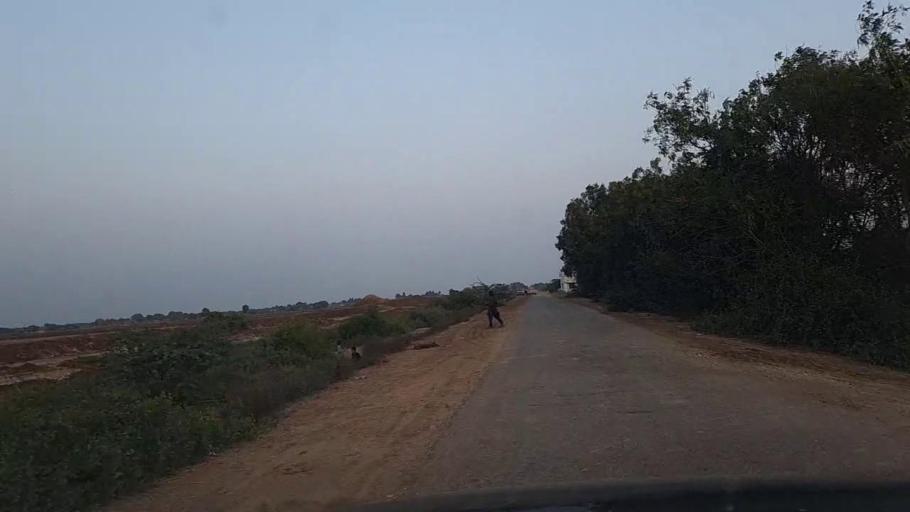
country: PK
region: Sindh
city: Mirpur Sakro
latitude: 24.6294
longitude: 67.6416
